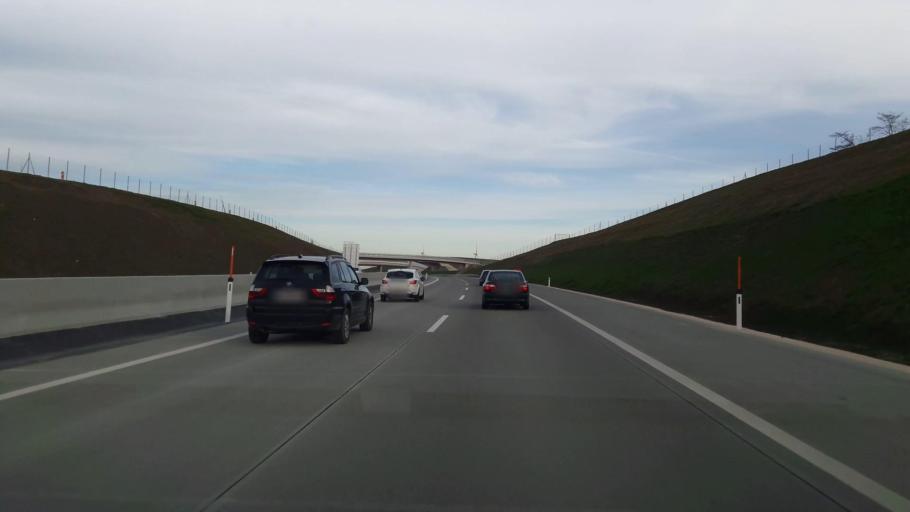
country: AT
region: Lower Austria
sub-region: Politischer Bezirk Mistelbach
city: Wilfersdorf
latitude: 48.6058
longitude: 16.6643
